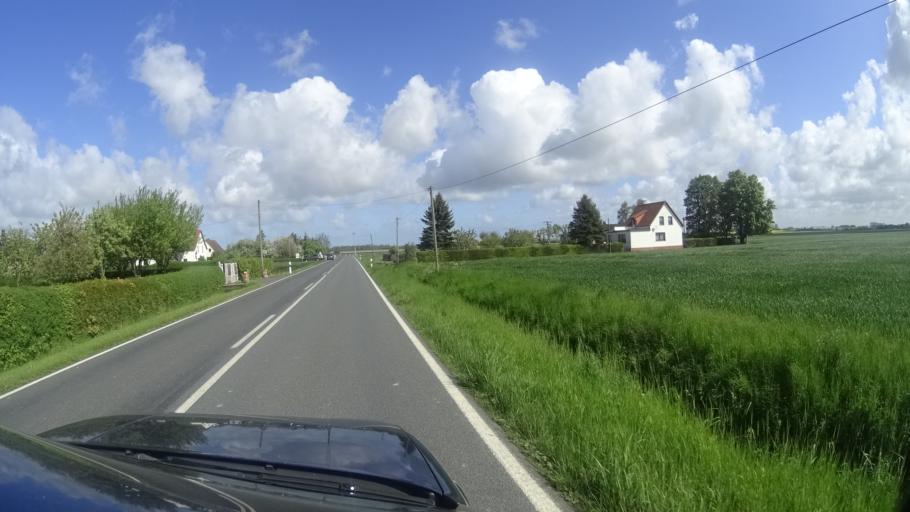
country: DE
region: Mecklenburg-Vorpommern
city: Trinwillershagen
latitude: 54.2828
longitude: 12.5902
